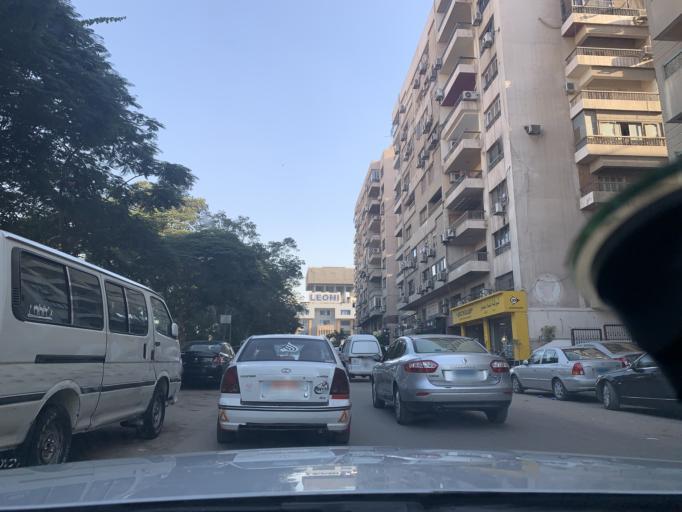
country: EG
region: Muhafazat al Qahirah
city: Cairo
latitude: 30.0365
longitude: 31.3466
